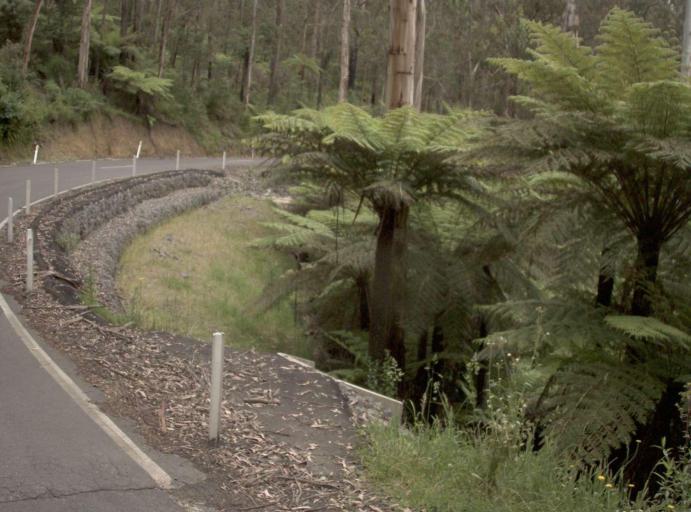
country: AU
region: Victoria
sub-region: Latrobe
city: Moe
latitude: -37.9358
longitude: 146.1120
